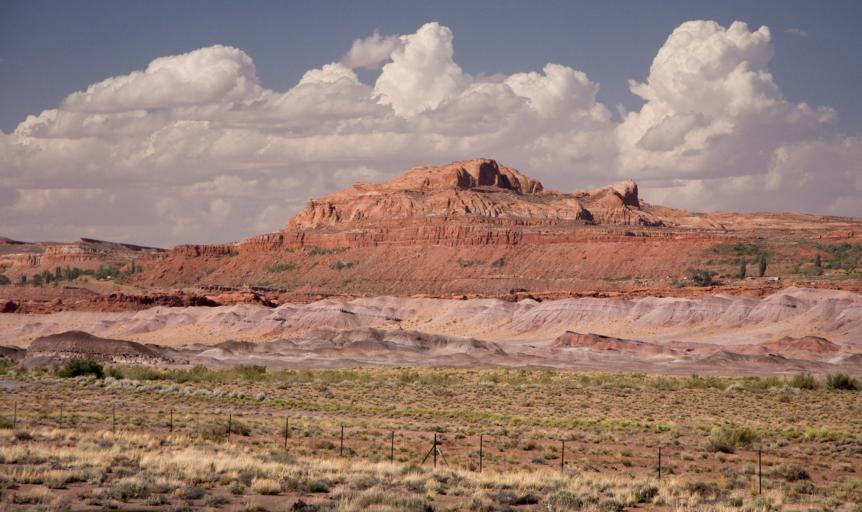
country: US
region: Arizona
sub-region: Coconino County
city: Tuba City
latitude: 36.1389
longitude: -111.3962
